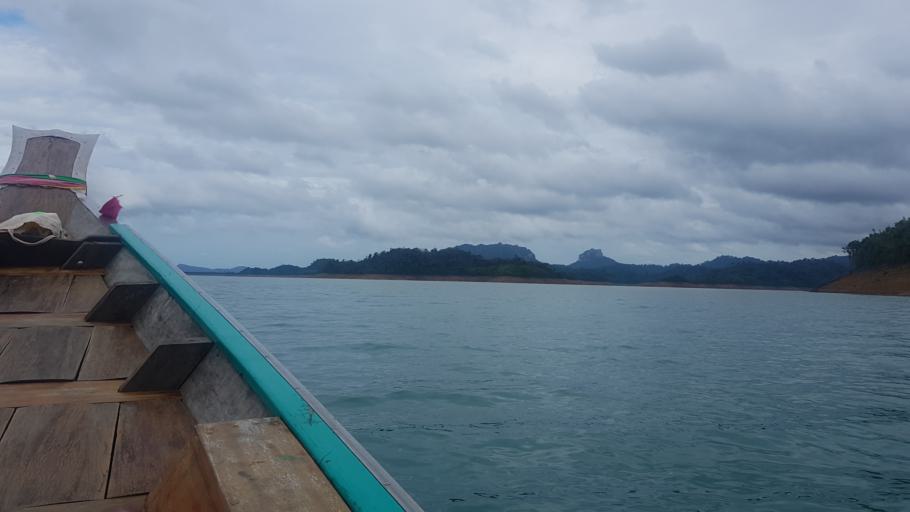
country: TH
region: Surat Thani
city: Phanom
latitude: 9.0070
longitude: 98.7592
